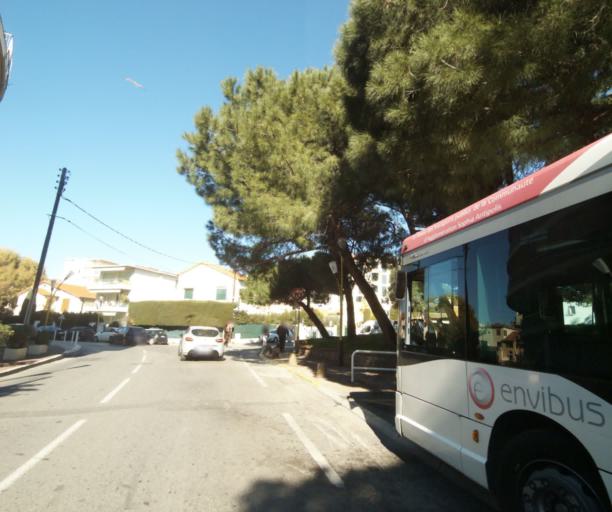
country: FR
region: Provence-Alpes-Cote d'Azur
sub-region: Departement des Alpes-Maritimes
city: Antibes
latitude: 43.5689
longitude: 7.1148
